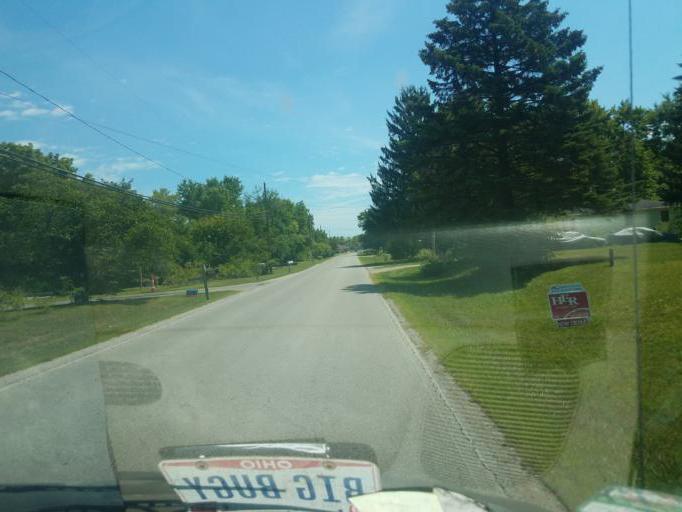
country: US
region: Ohio
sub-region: Franklin County
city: Grove City
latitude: 39.8719
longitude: -83.0887
